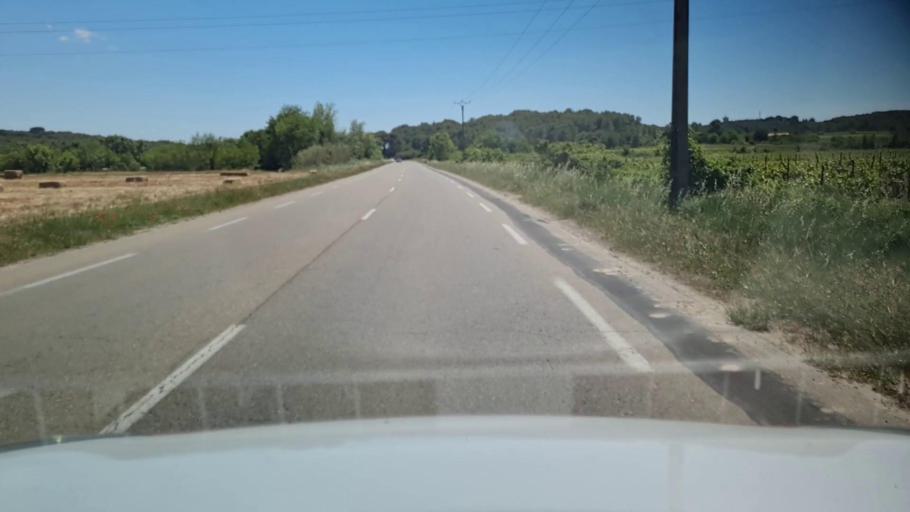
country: FR
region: Languedoc-Roussillon
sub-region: Departement du Gard
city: Mus
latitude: 43.7560
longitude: 4.2047
